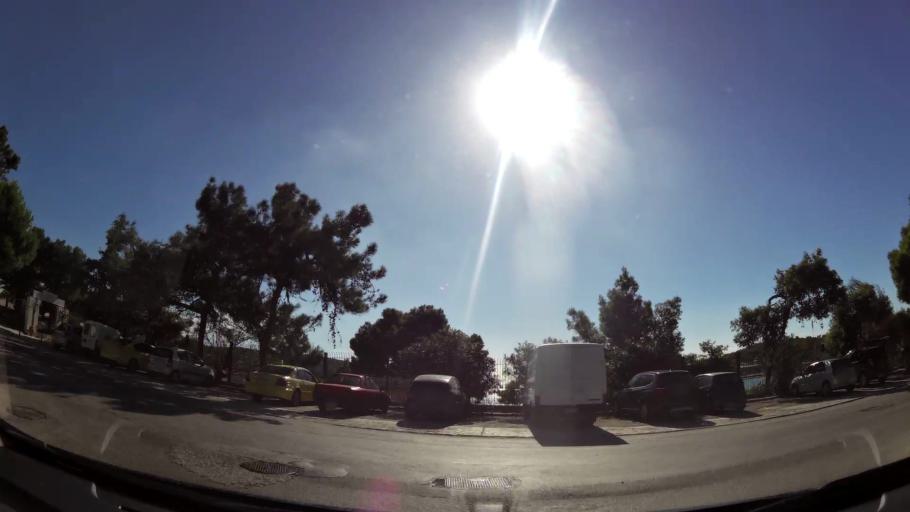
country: GR
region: Attica
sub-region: Nomarchia Anatolikis Attikis
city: Vouliagmeni
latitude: 37.8126
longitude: 23.7752
